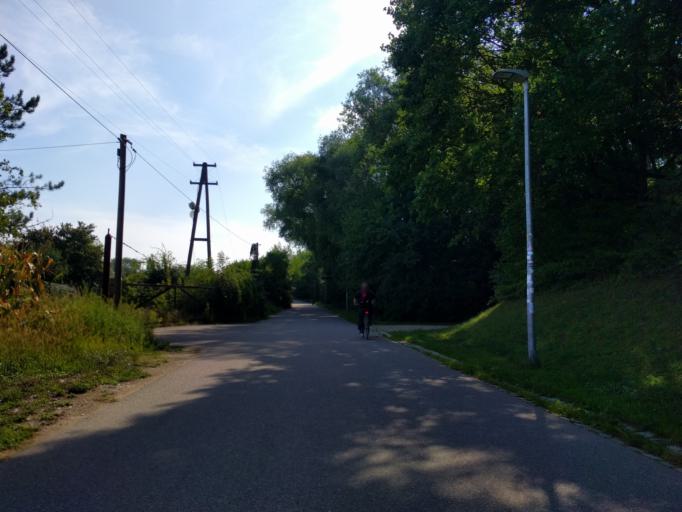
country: DE
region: Bavaria
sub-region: Upper Palatinate
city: Regensburg
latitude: 49.0239
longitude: 12.1258
